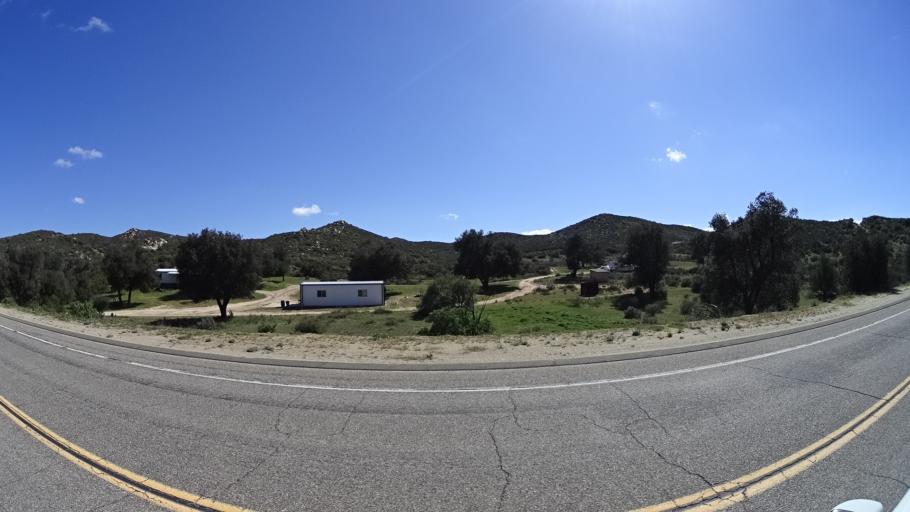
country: US
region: California
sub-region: San Diego County
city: Julian
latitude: 33.2106
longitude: -116.5446
